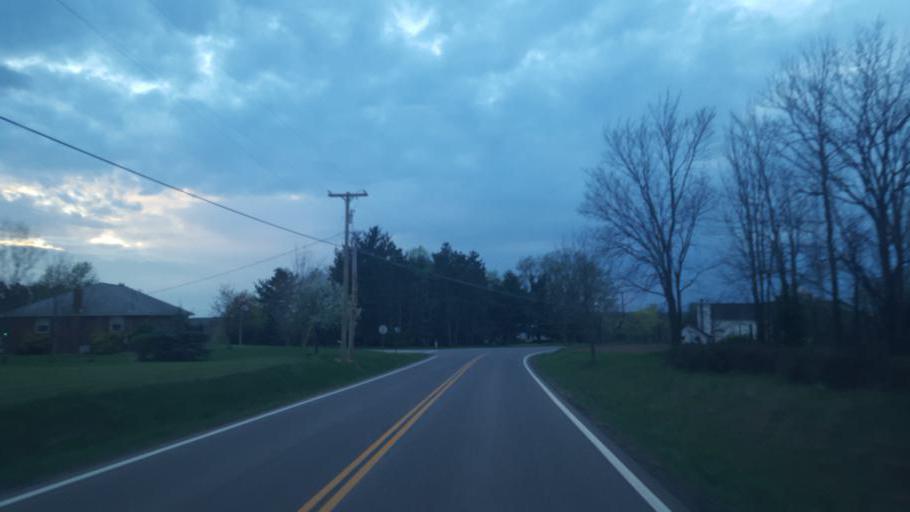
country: US
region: Ohio
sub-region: Ashland County
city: Ashland
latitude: 40.8731
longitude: -82.4119
